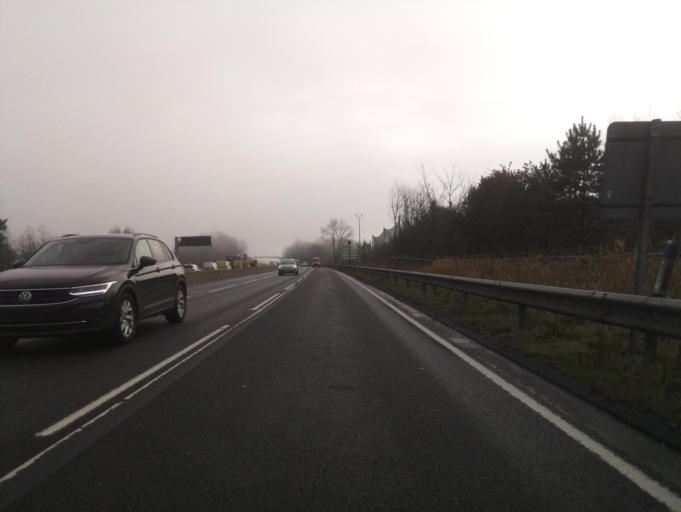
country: GB
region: England
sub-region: Borough of Wigan
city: Ashton in Makerfield
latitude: 53.4833
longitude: -2.6492
